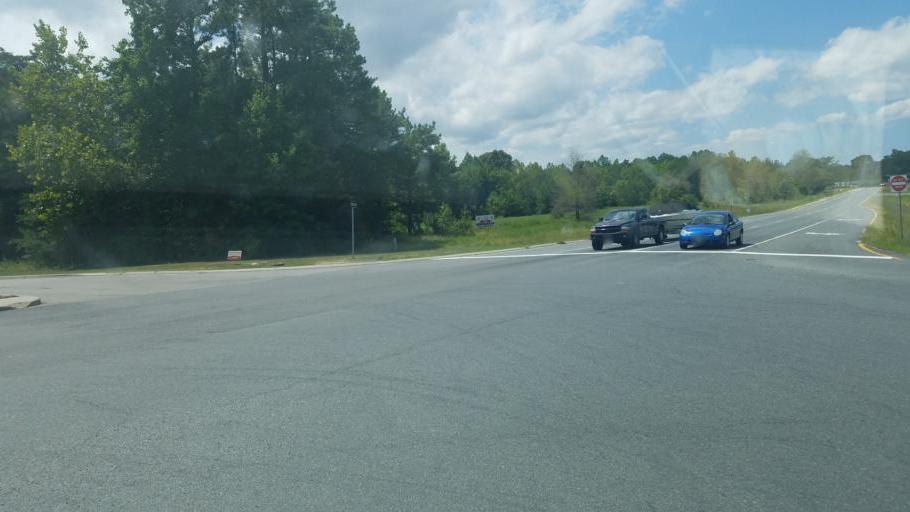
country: US
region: Virginia
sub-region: Caroline County
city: Bowling Green
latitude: 37.9340
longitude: -77.4748
